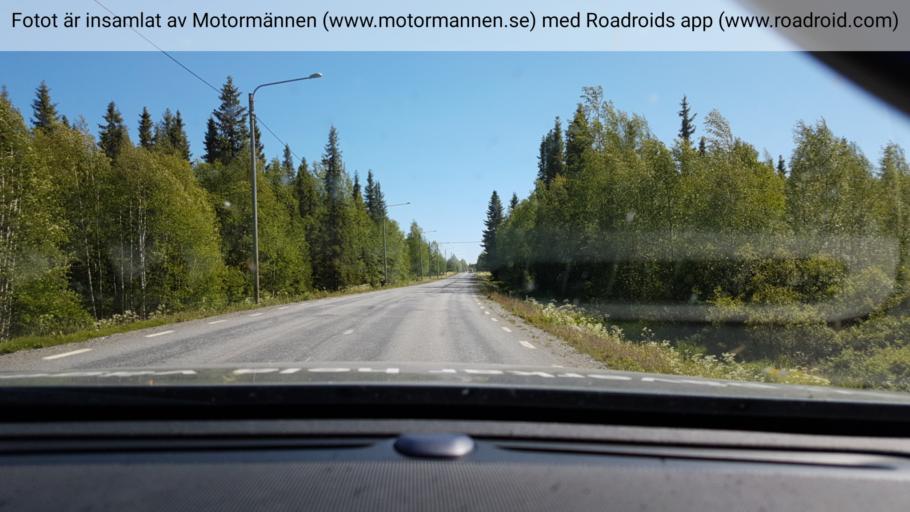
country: SE
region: Vaesterbotten
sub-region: Vilhelmina Kommun
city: Sjoberg
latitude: 64.6817
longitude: 16.2883
